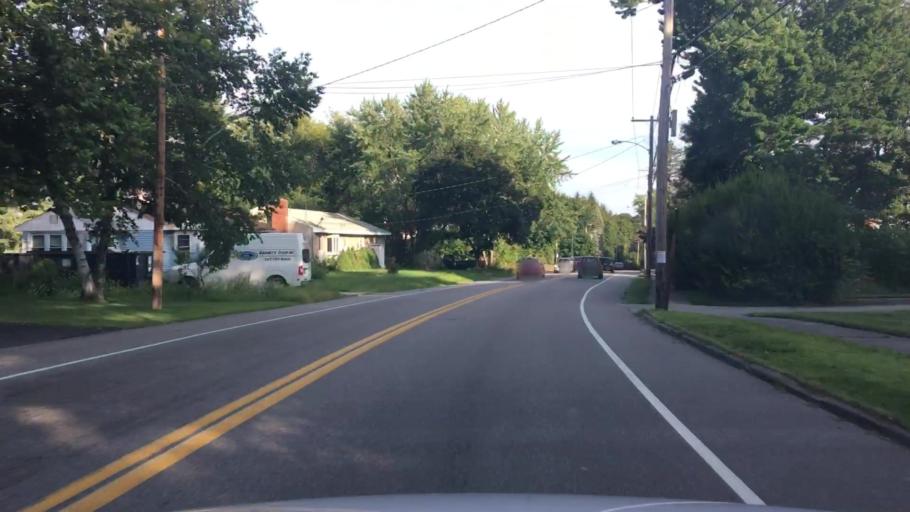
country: US
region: Maine
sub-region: Cumberland County
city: Westbrook
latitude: 43.6881
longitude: -70.3600
